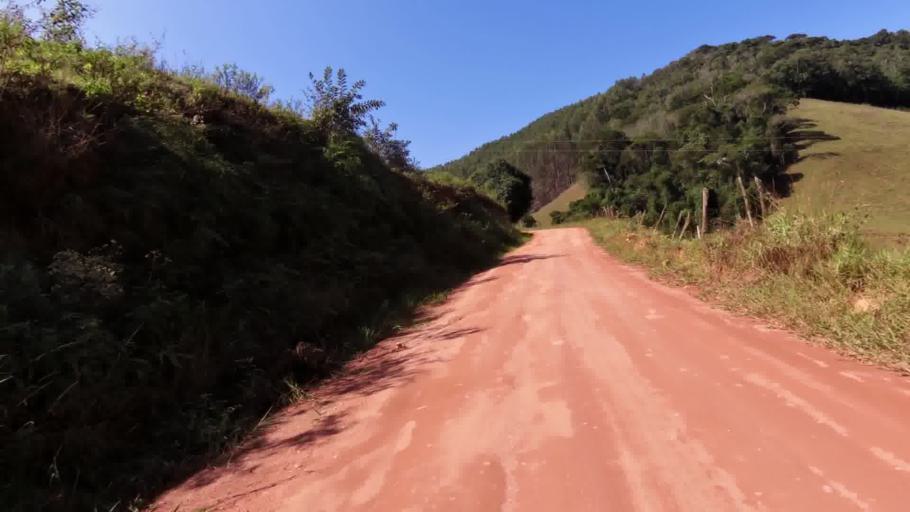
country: BR
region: Espirito Santo
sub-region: Alfredo Chaves
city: Alfredo Chaves
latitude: -20.5680
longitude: -40.7787
